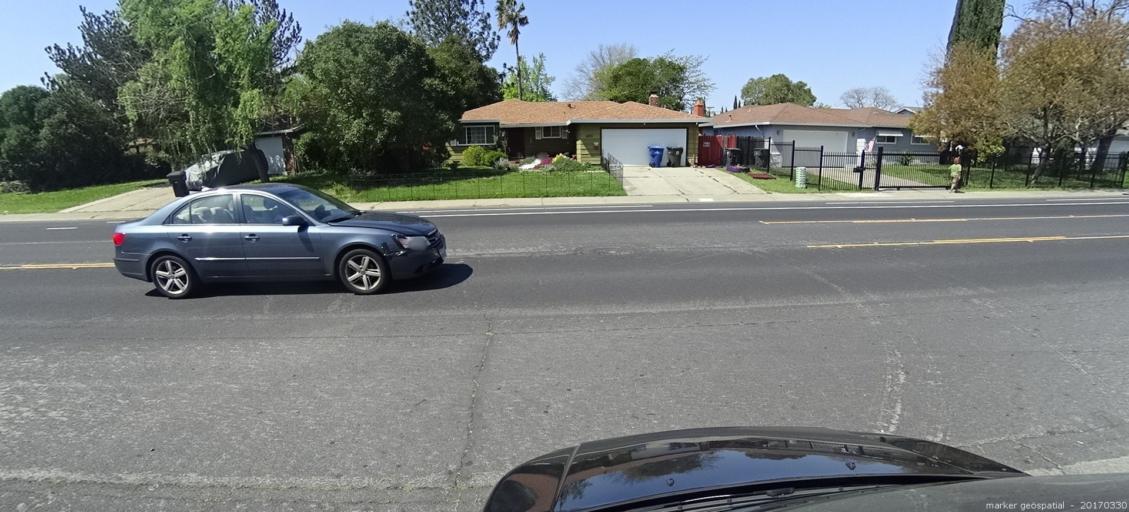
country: US
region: California
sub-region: Sacramento County
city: Florin
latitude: 38.4654
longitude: -121.4277
